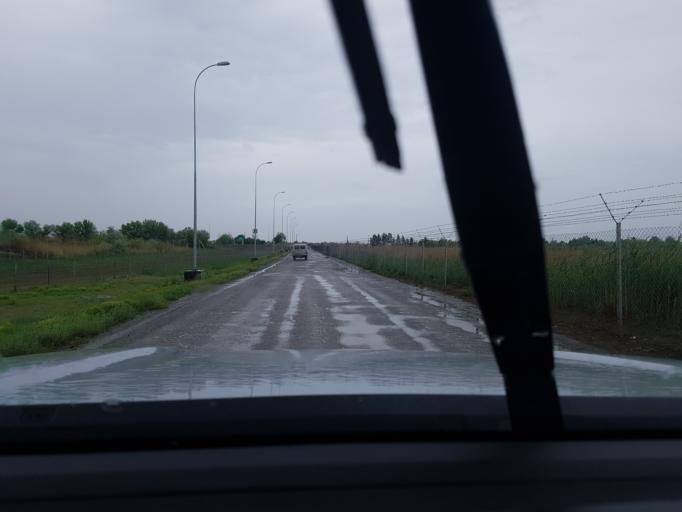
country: TM
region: Lebap
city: Farap
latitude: 39.2167
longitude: 63.7138
